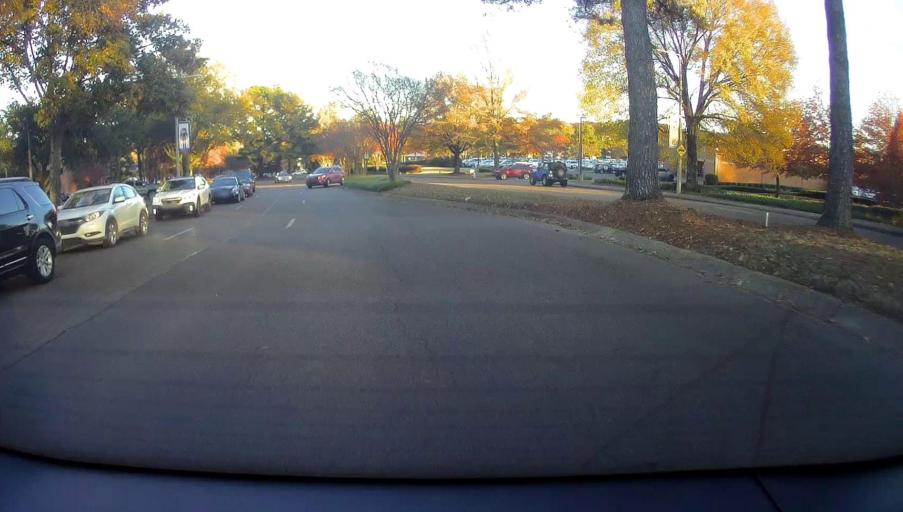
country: US
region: Tennessee
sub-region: Shelby County
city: Germantown
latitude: 35.0955
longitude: -89.8068
